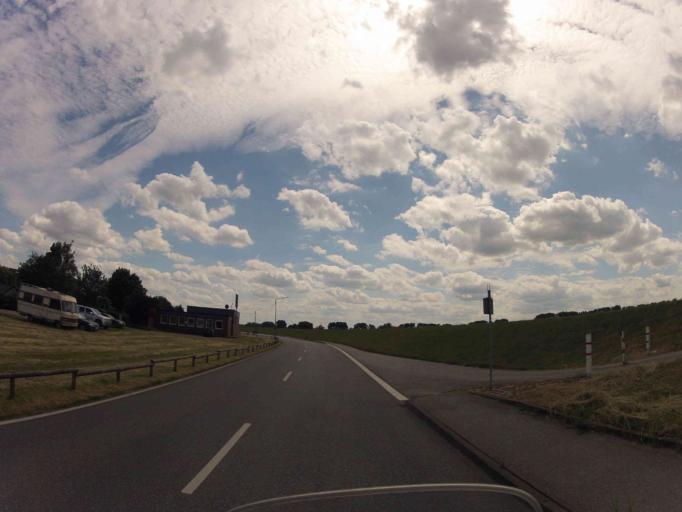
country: DE
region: Hamburg
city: Rothenburgsort
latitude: 53.4870
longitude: 10.0541
